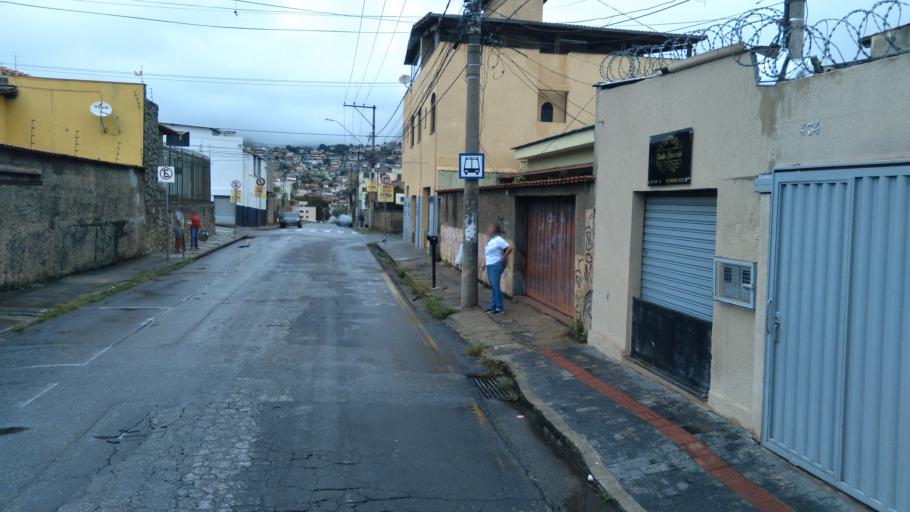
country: BR
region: Minas Gerais
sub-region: Belo Horizonte
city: Belo Horizonte
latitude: -19.9133
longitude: -43.9046
